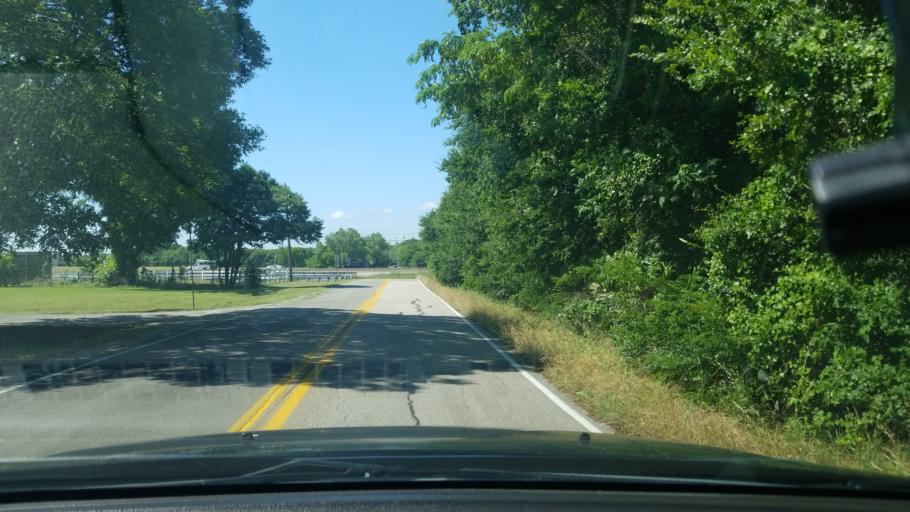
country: US
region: Texas
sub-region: Dallas County
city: Sunnyvale
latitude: 32.7851
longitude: -96.5550
